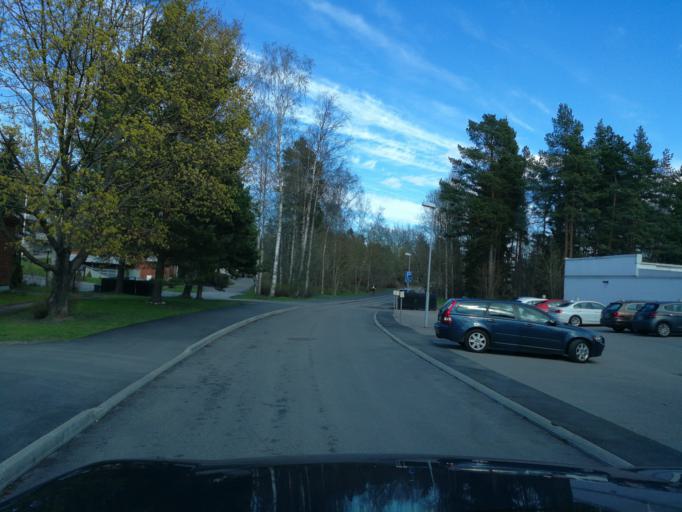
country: FI
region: Uusimaa
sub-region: Helsinki
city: Koukkuniemi
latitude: 60.1637
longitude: 24.7653
